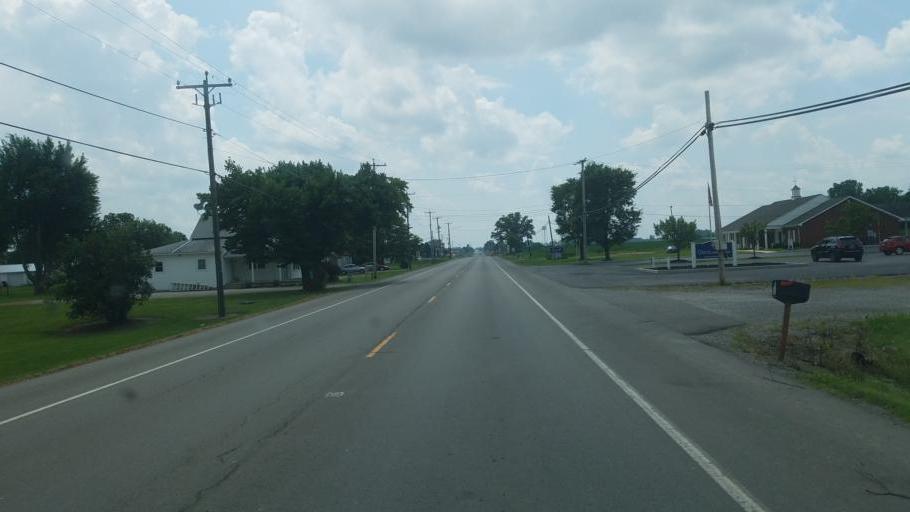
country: US
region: Ohio
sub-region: Hardin County
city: Kenton
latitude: 40.6346
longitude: -83.6138
